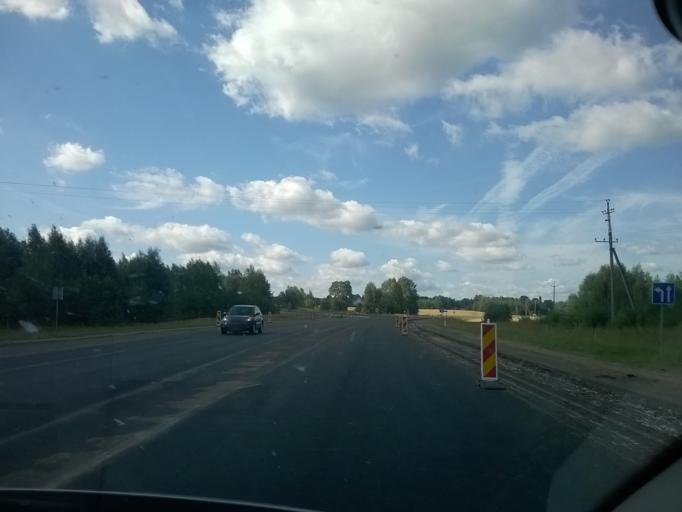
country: EE
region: Vorumaa
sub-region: Voru linn
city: Voru
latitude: 57.7955
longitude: 26.9558
